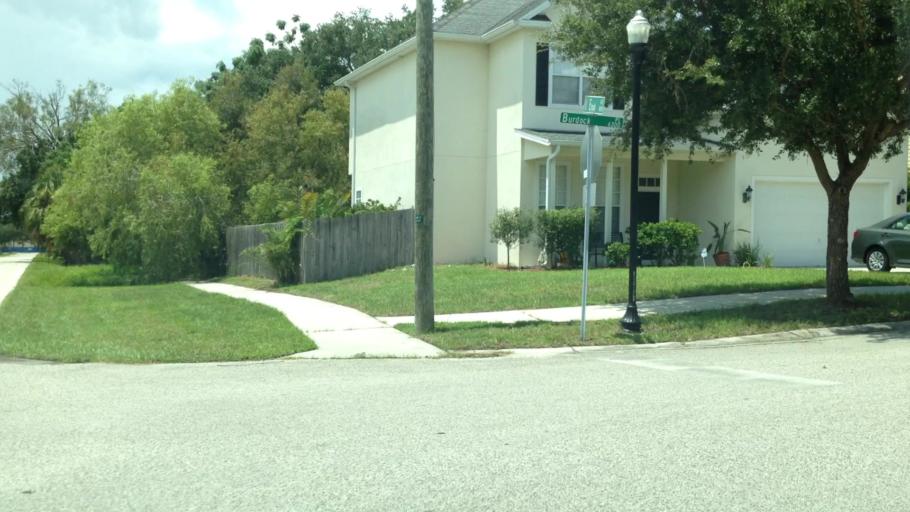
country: US
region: Florida
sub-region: Hillsborough County
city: Tampa
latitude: 27.8737
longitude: -82.5109
